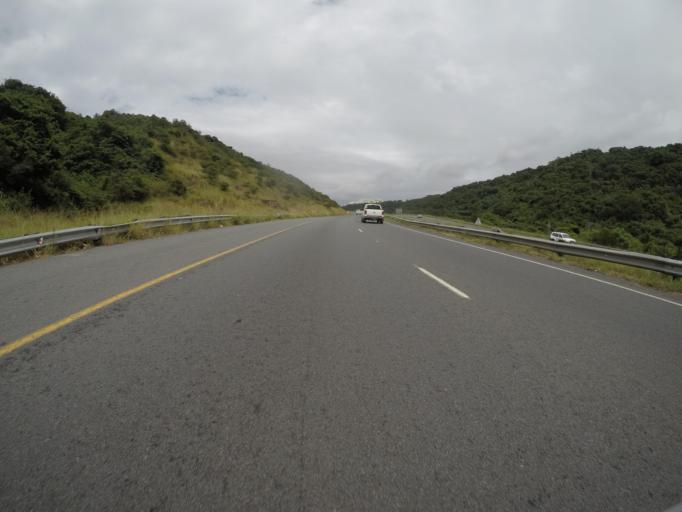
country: ZA
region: Eastern Cape
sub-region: Buffalo City Metropolitan Municipality
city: East London
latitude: -32.9686
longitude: 27.9148
